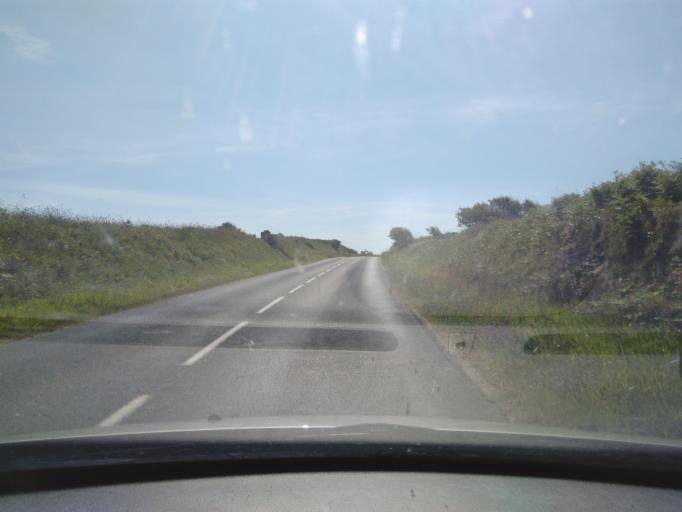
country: FR
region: Lower Normandy
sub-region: Departement de la Manche
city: Beaumont-Hague
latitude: 49.6971
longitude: -1.9236
